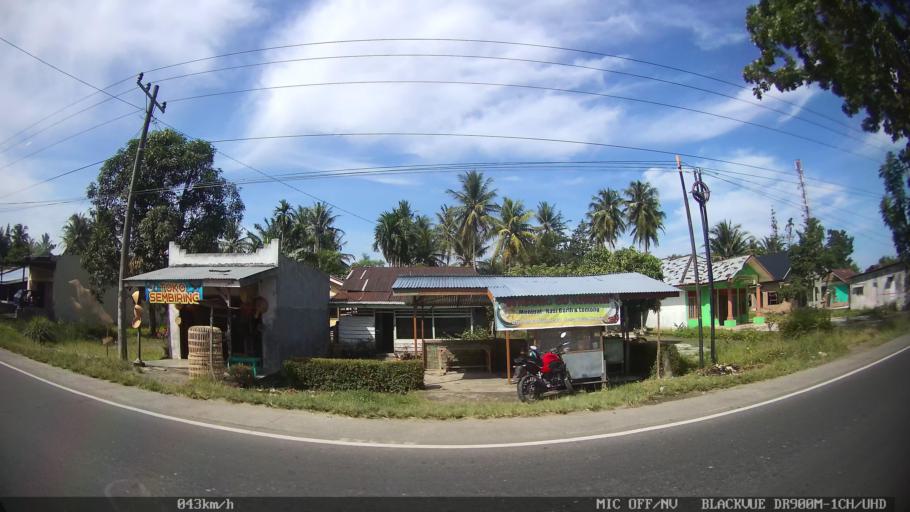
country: ID
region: North Sumatra
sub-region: Kabupaten Langkat
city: Stabat
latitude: 3.7269
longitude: 98.4972
